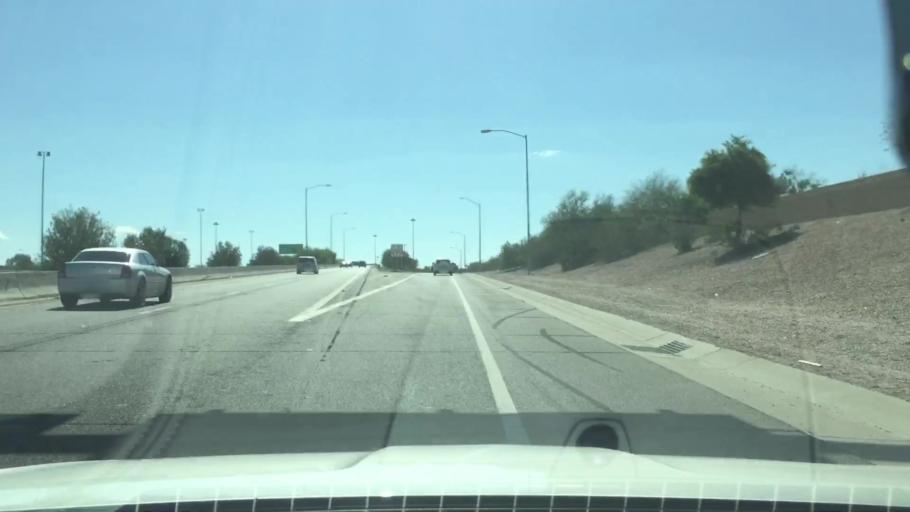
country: US
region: Arizona
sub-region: Maricopa County
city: Tempe
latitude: 33.3917
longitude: -111.8916
